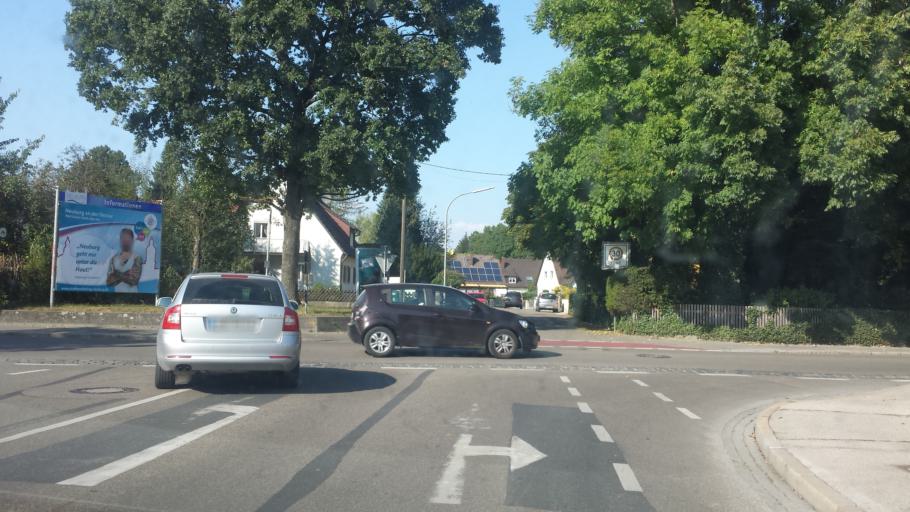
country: DE
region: Bavaria
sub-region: Upper Bavaria
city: Neuburg an der Donau
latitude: 48.7371
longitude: 11.1979
